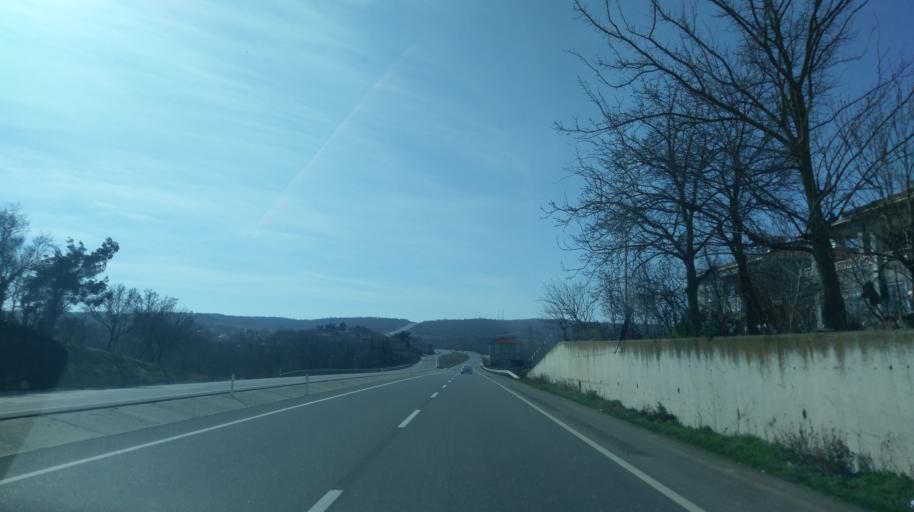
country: TR
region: Edirne
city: Ibriktepe
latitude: 40.9945
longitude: 26.6375
